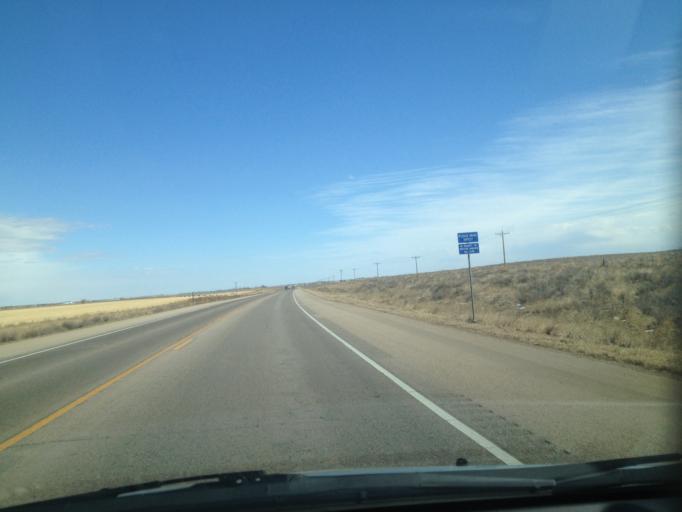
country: US
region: Colorado
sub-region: Weld County
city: Kersey
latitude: 40.2935
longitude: -104.2904
